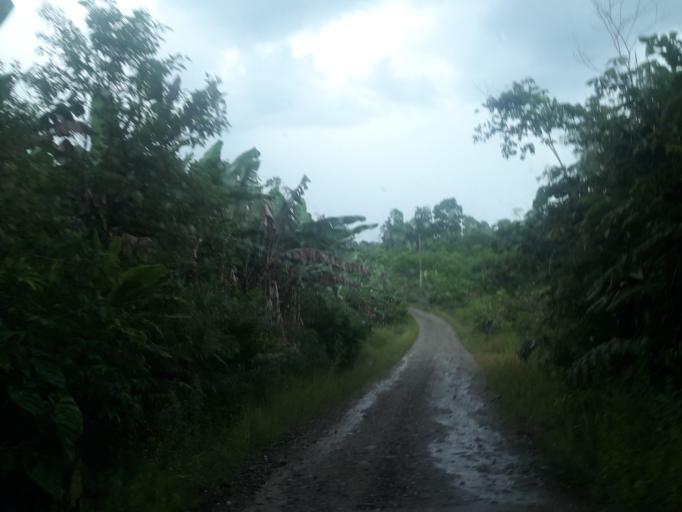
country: EC
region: Napo
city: Tena
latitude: -1.0928
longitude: -77.7017
